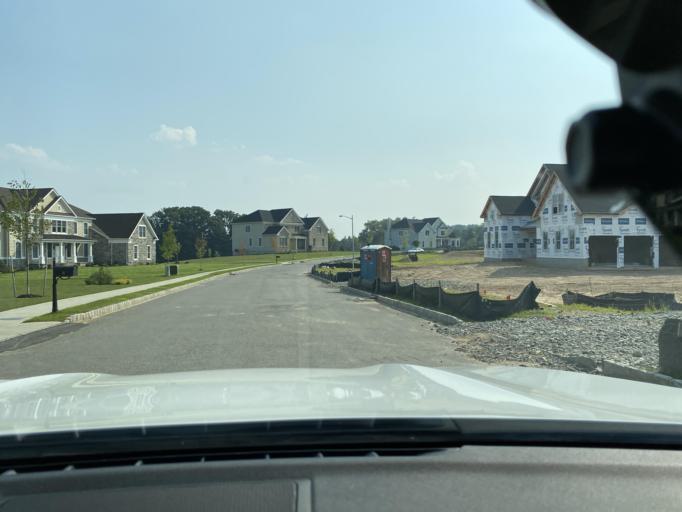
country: US
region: New Jersey
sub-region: Bergen County
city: Upper Saddle River
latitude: 41.0752
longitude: -74.1162
